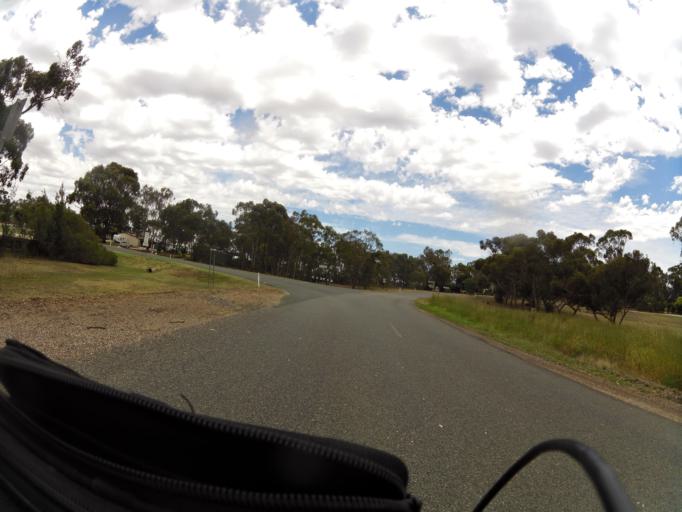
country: AU
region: Victoria
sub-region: Campaspe
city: Kyabram
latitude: -36.7416
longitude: 145.1349
